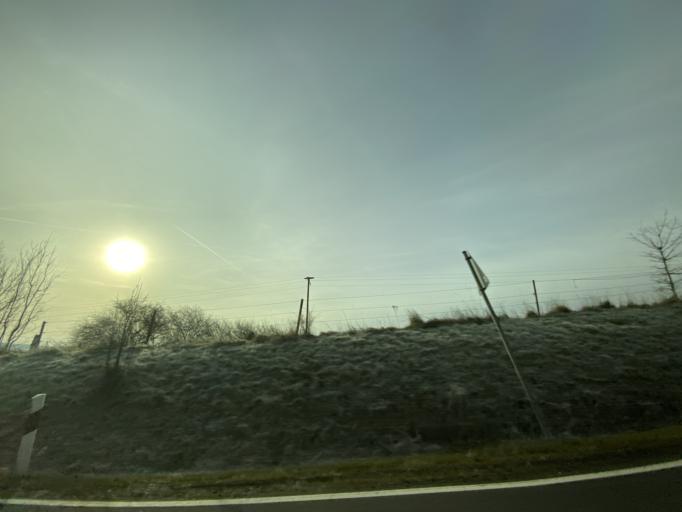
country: DE
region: Hesse
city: Amoneburg
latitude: 50.7902
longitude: 8.9188
